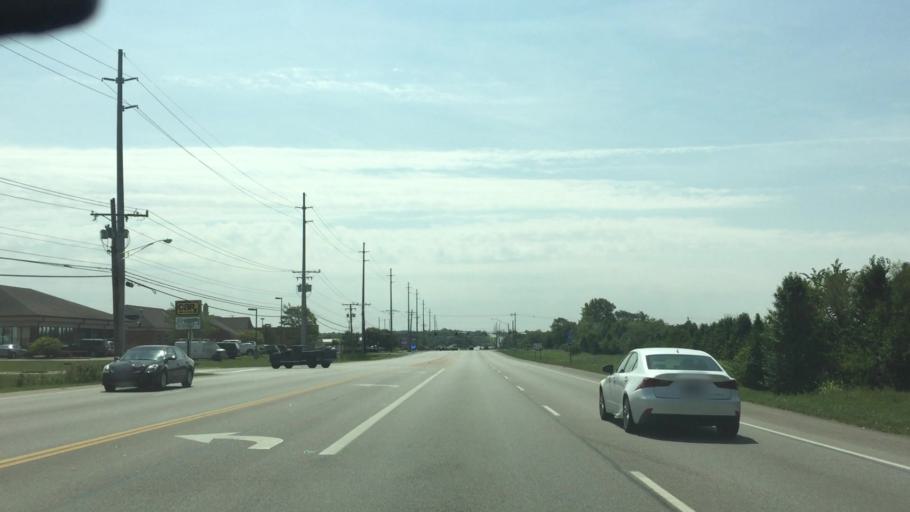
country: US
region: Ohio
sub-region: Butler County
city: Beckett Ridge
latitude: 39.3458
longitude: -84.4615
